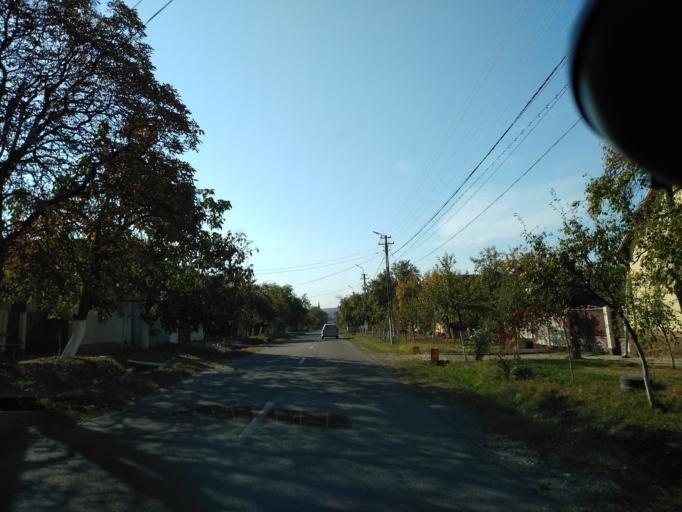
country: RO
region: Timis
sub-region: Oras Recas
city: Recas
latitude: 45.8645
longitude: 21.5147
